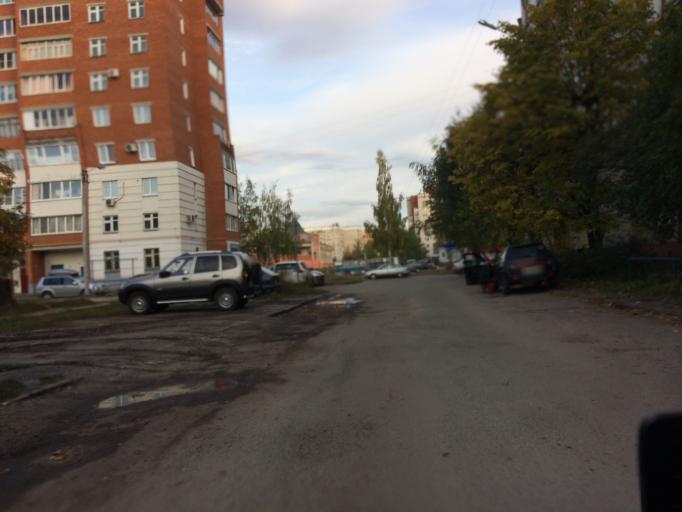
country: RU
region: Mariy-El
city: Yoshkar-Ola
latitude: 56.6333
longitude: 47.9180
